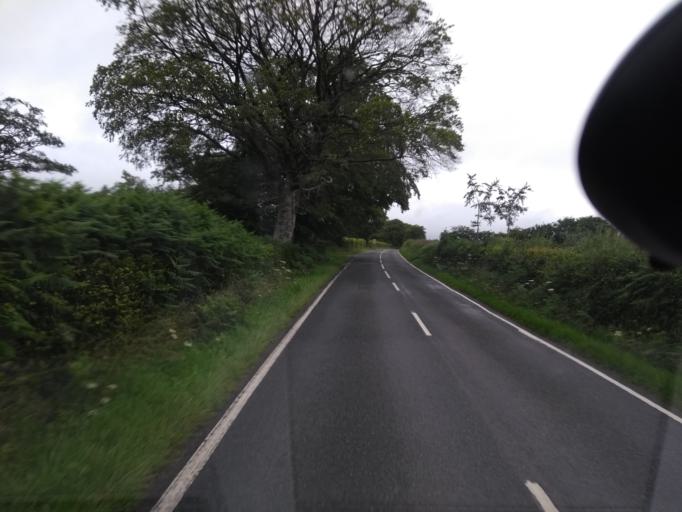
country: GB
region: England
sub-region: Somerset
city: Taunton
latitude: 50.9364
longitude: -3.1001
